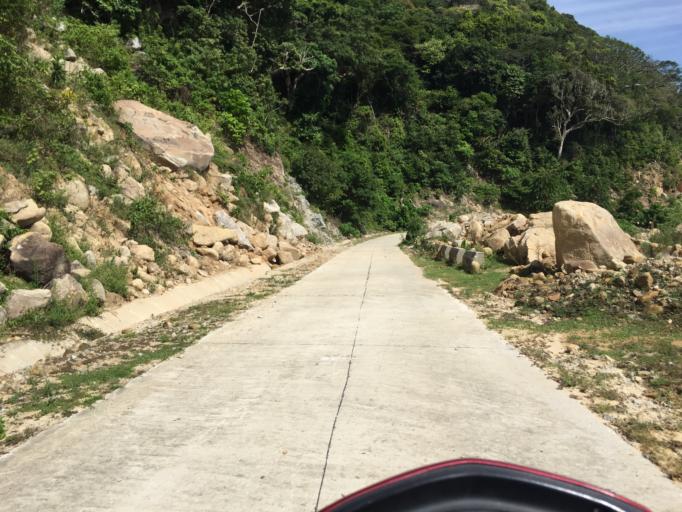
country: VN
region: Quang Nam
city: Hoi An
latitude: 15.9460
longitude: 108.5309
